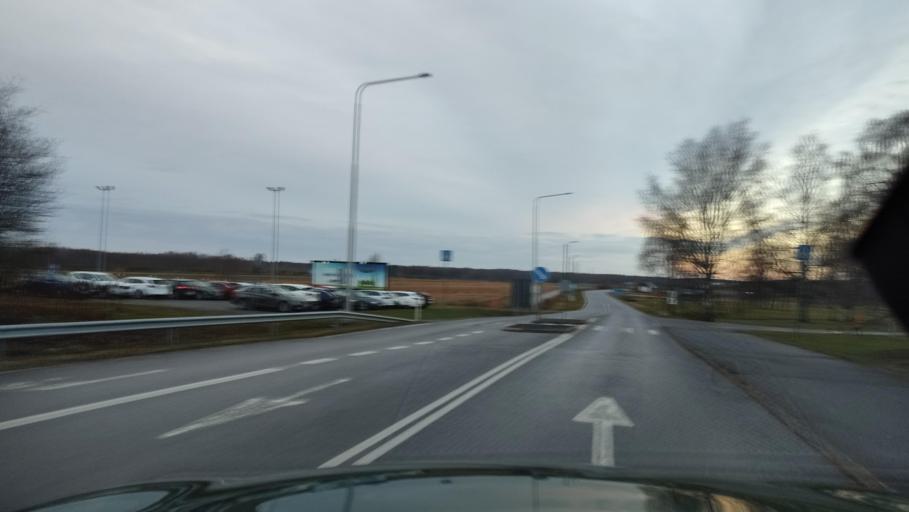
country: FI
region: Ostrobothnia
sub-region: Vaasa
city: Ristinummi
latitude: 63.0432
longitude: 21.7586
